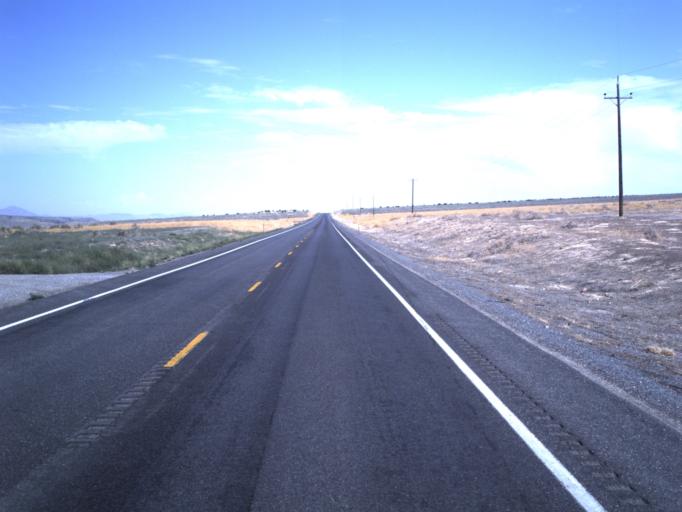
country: US
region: Utah
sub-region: Sanpete County
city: Gunnison
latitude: 39.2679
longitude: -111.8702
